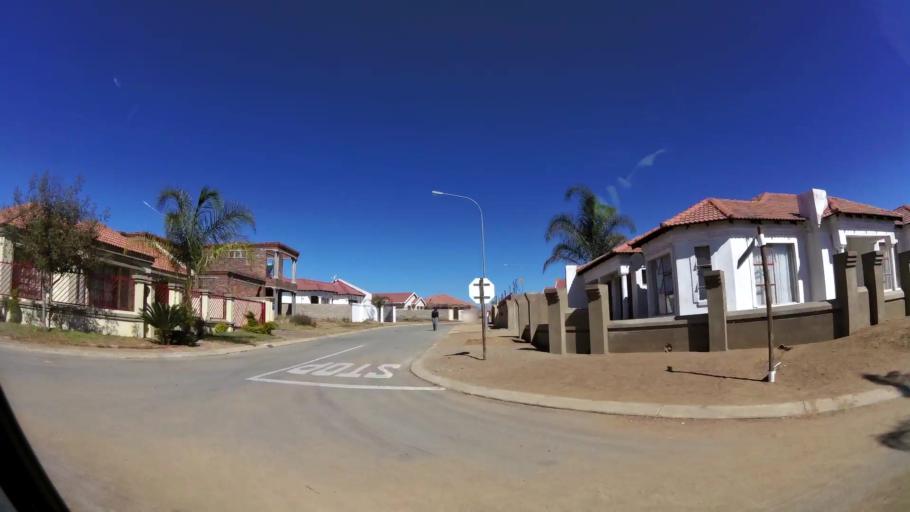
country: ZA
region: Limpopo
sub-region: Capricorn District Municipality
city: Polokwane
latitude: -23.8689
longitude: 29.4187
